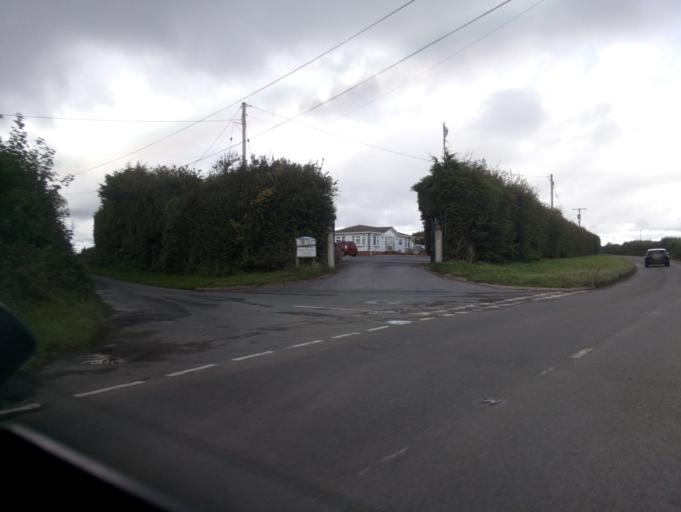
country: GB
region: England
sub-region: Devon
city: Kingsbridge
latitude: 50.2993
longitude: -3.7919
